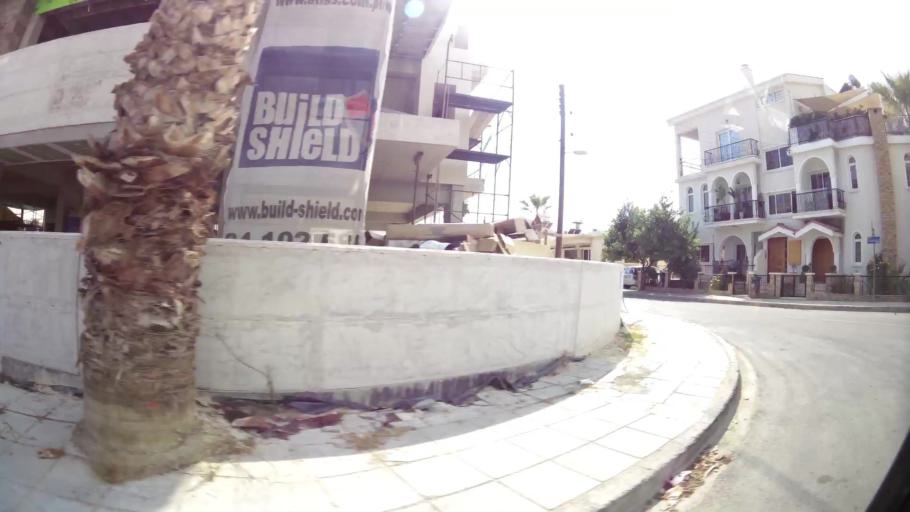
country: CY
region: Larnaka
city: Larnaca
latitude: 34.9200
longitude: 33.6051
